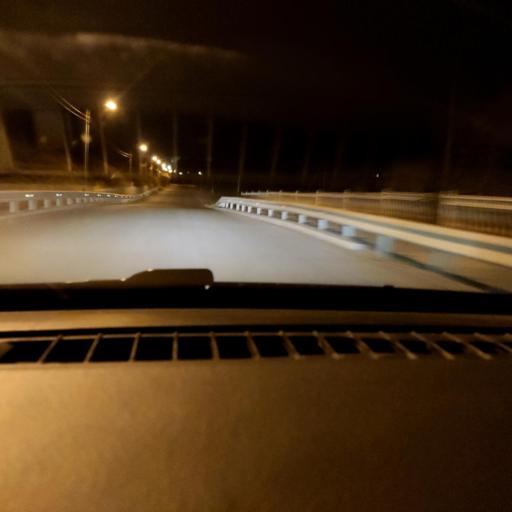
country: RU
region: Voronezj
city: Pridonskoy
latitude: 51.6649
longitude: 39.0880
